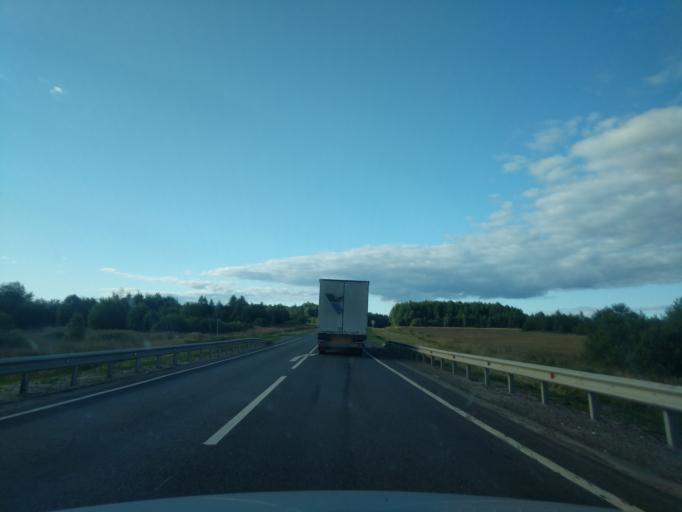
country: RU
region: Kostroma
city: Manturovo
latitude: 58.3098
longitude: 44.7229
